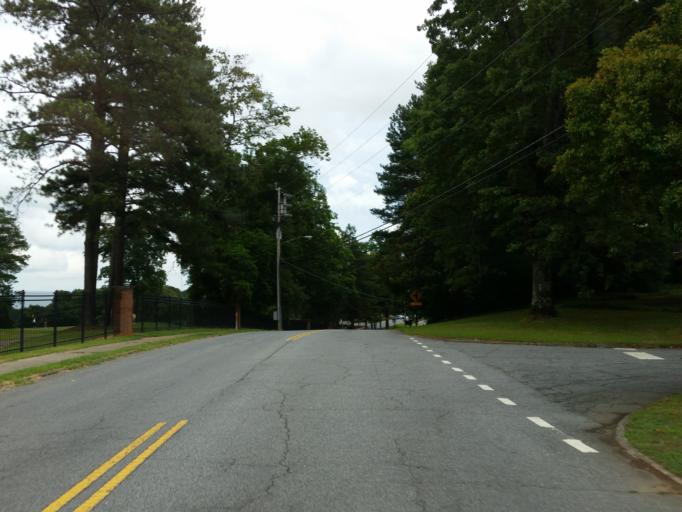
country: US
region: Georgia
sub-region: Cobb County
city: Kennesaw
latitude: 34.0387
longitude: -84.5953
